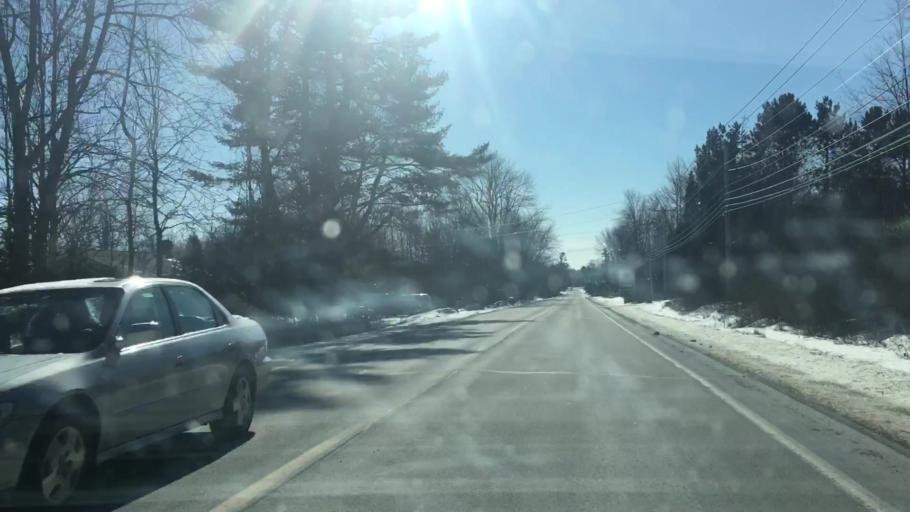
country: US
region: Maine
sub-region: Hancock County
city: Ellsworth
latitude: 44.5048
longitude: -68.4404
